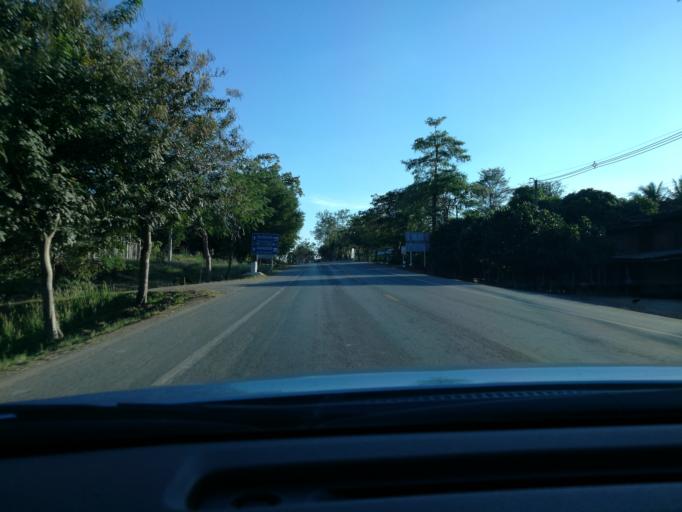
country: TH
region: Phitsanulok
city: Nakhon Thai
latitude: 17.0594
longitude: 100.8097
